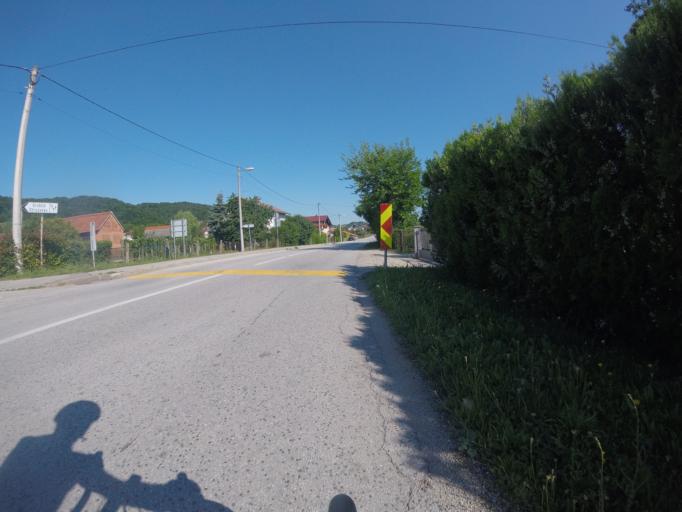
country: HR
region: Zagrebacka
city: Bregana
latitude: 45.8308
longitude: 15.6910
